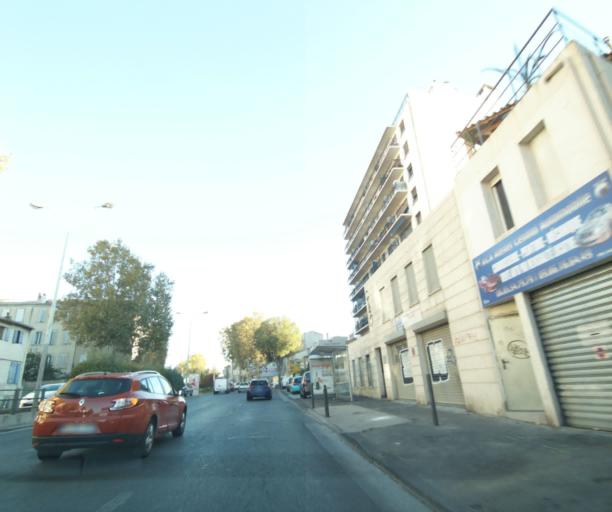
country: FR
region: Provence-Alpes-Cote d'Azur
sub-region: Departement des Bouches-du-Rhone
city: Marseille 04
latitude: 43.3081
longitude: 5.4023
